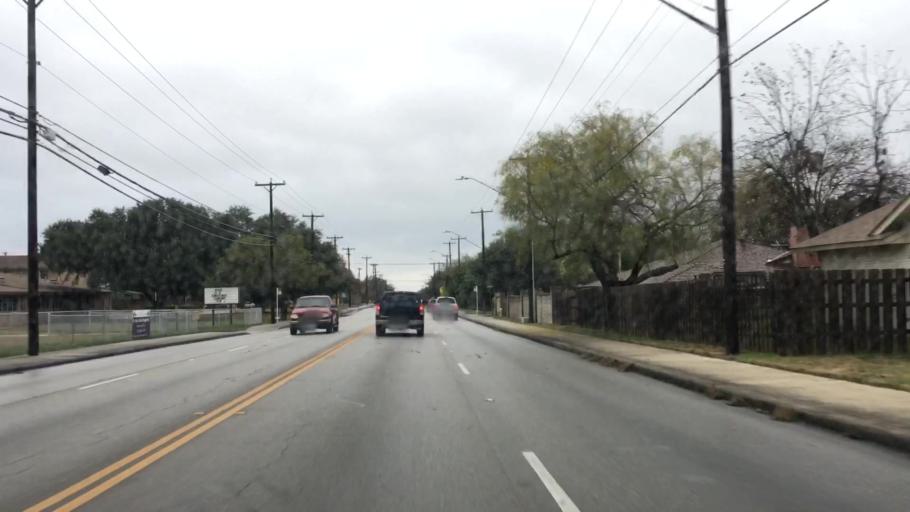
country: US
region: Texas
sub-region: Bexar County
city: Castle Hills
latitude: 29.5090
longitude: -98.5069
